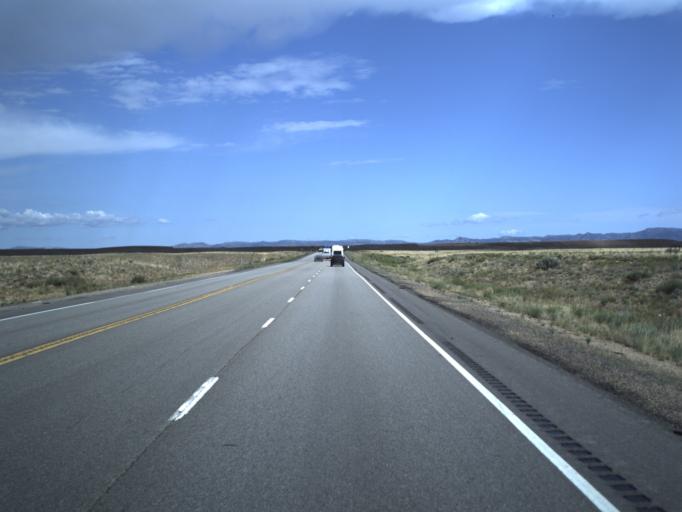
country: US
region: Utah
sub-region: Carbon County
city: East Carbon City
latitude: 39.4865
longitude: -110.5150
